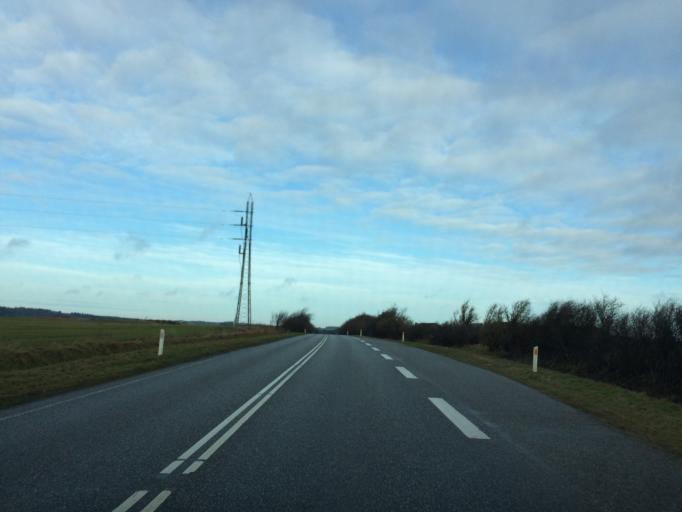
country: DK
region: Central Jutland
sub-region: Struer Kommune
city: Struer
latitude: 56.4796
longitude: 8.5538
